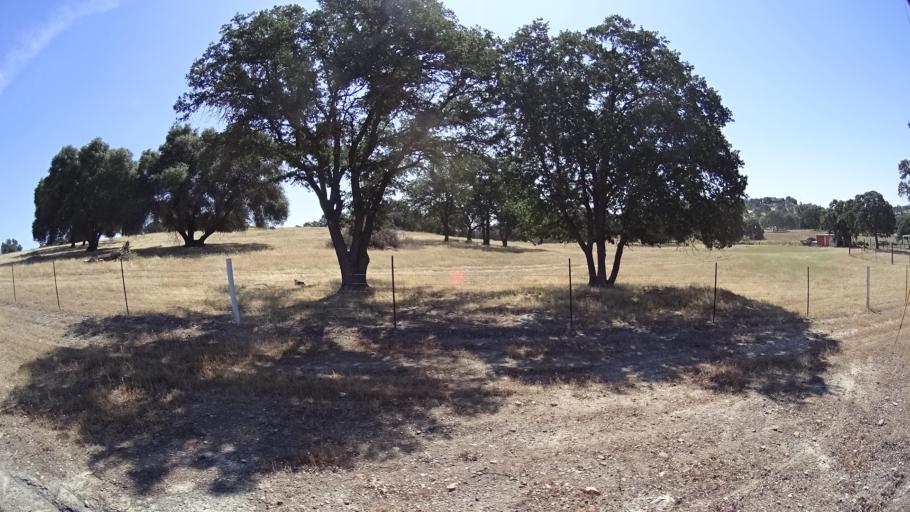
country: US
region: California
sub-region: Calaveras County
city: Rancho Calaveras
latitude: 38.1200
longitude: -120.9265
